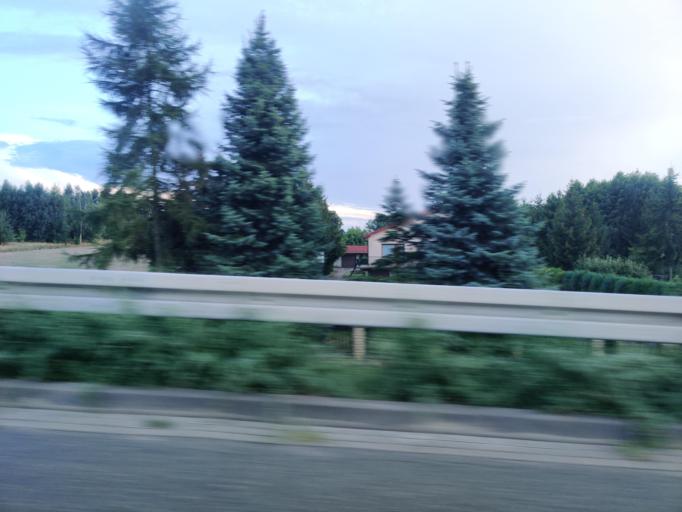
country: PL
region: Greater Poland Voivodeship
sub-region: Konin
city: Konin
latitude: 52.1958
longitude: 18.3076
